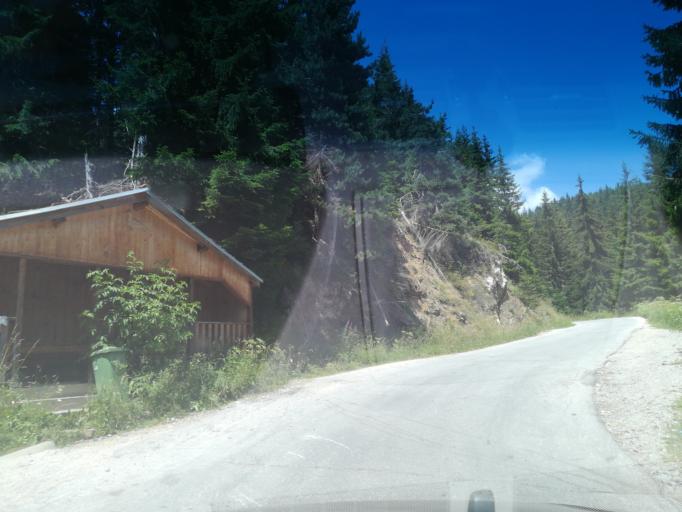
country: BG
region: Smolyan
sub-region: Obshtina Chepelare
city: Chepelare
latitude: 41.6900
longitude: 24.7710
